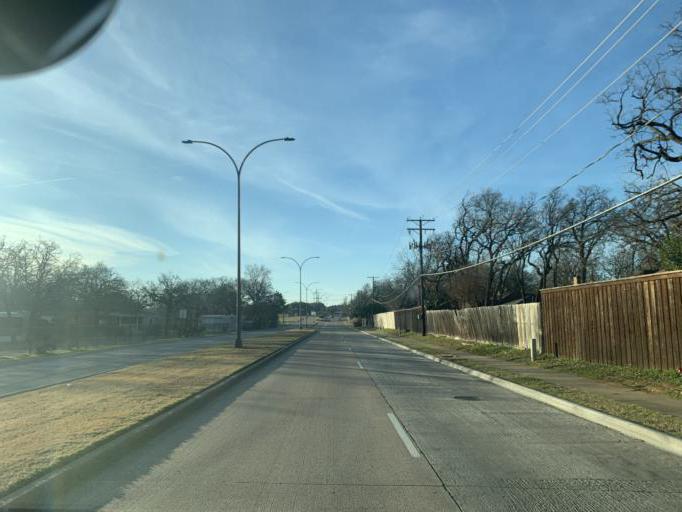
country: US
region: Texas
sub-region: Tarrant County
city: Arlington
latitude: 32.7690
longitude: -97.0738
